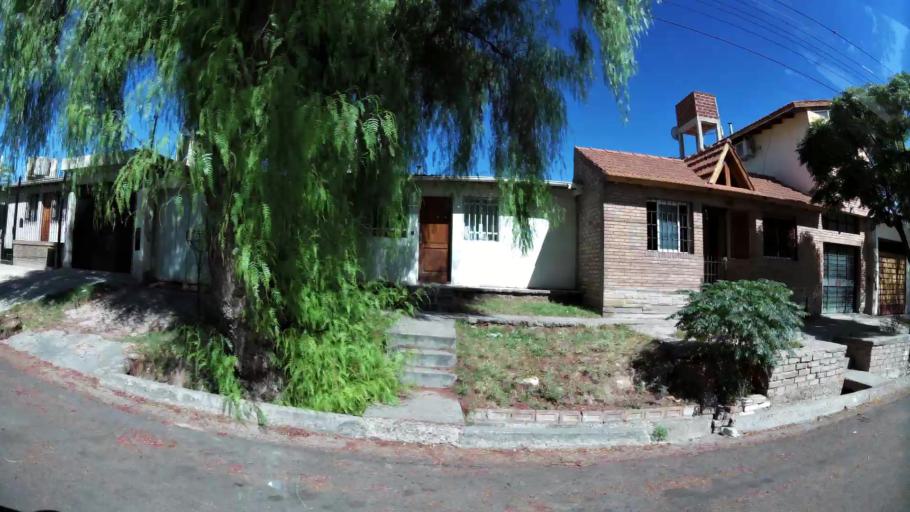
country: AR
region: Mendoza
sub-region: Departamento de Godoy Cruz
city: Godoy Cruz
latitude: -32.9134
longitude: -68.8794
